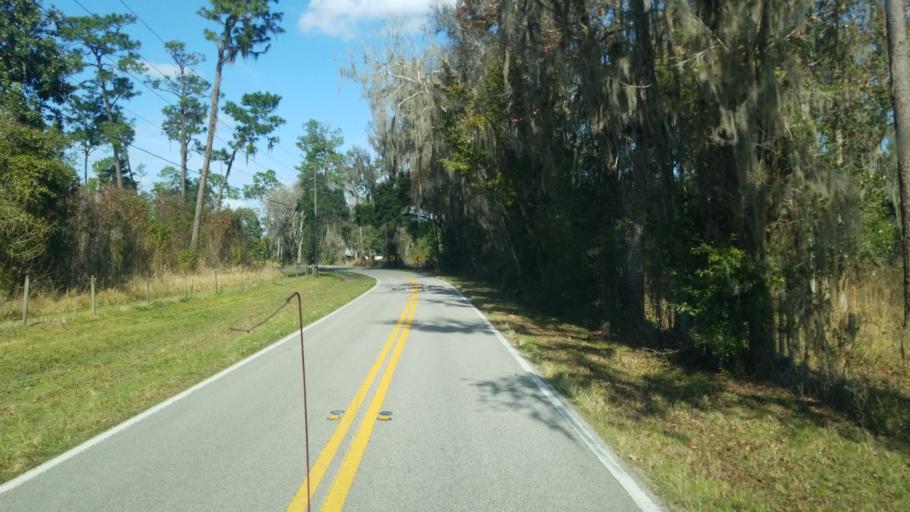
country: US
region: Florida
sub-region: Hernando County
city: North Brooksville
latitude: 28.6058
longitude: -82.3792
